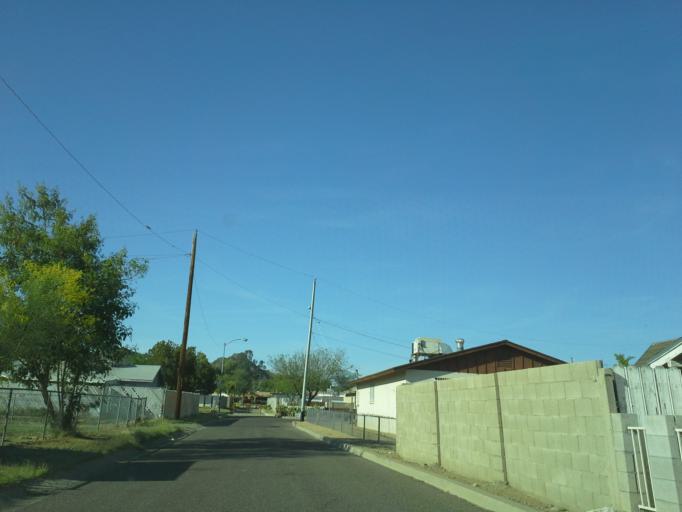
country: US
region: Arizona
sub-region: Maricopa County
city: Paradise Valley
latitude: 33.5769
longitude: -112.0588
